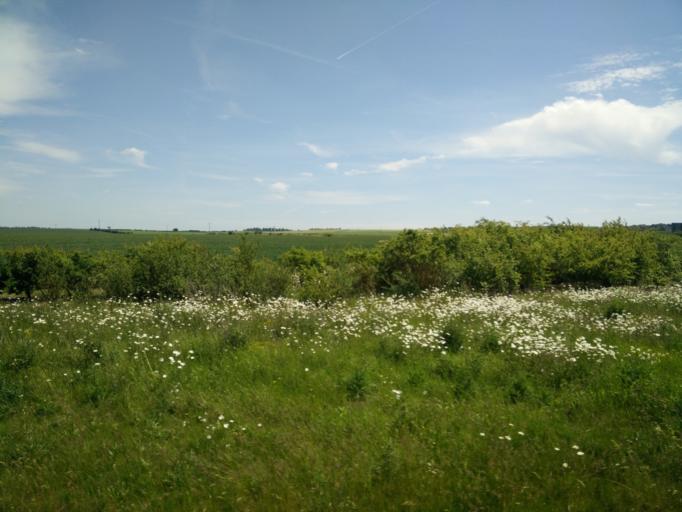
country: GB
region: England
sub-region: Hertfordshire
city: Baldock
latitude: 51.9947
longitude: -0.1604
